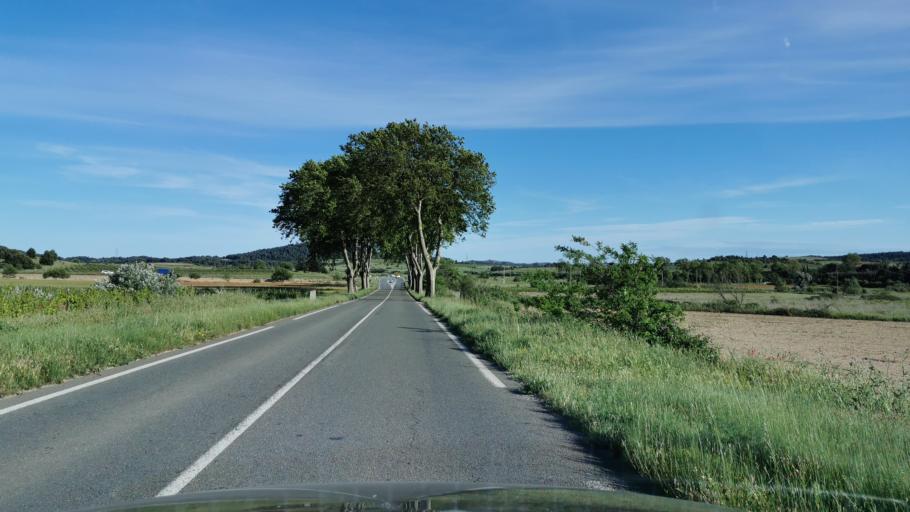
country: FR
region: Languedoc-Roussillon
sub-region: Departement de l'Aude
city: Marcorignan
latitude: 43.2199
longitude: 2.9267
